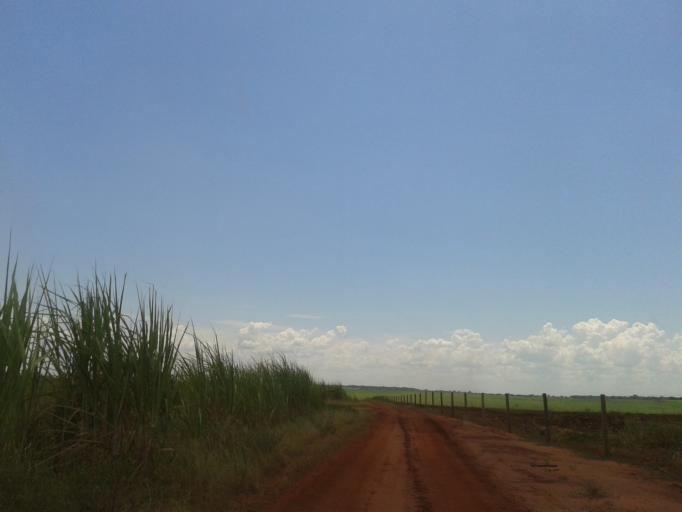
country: BR
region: Minas Gerais
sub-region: Santa Vitoria
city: Santa Vitoria
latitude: -19.1662
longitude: -50.4225
